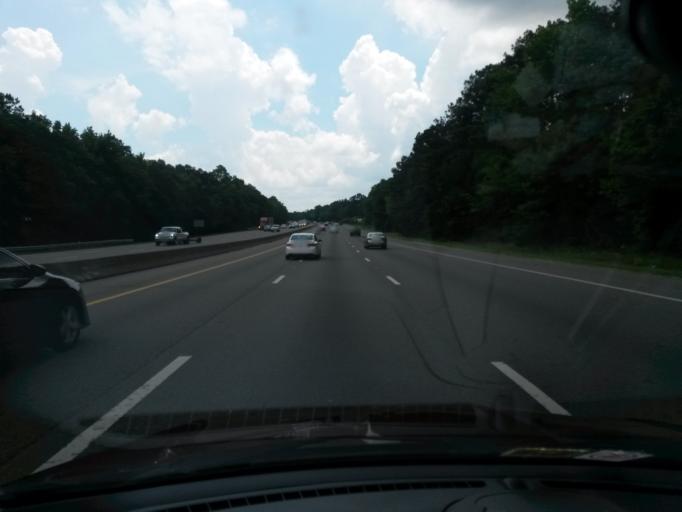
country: US
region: Virginia
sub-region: Chesterfield County
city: Bellwood
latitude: 37.3980
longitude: -77.4242
